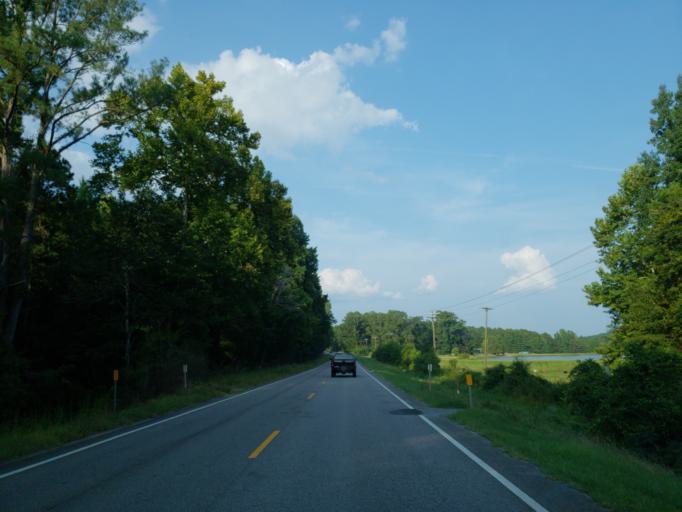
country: US
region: Alabama
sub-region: Greene County
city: Eutaw
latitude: 32.9309
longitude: -87.8186
